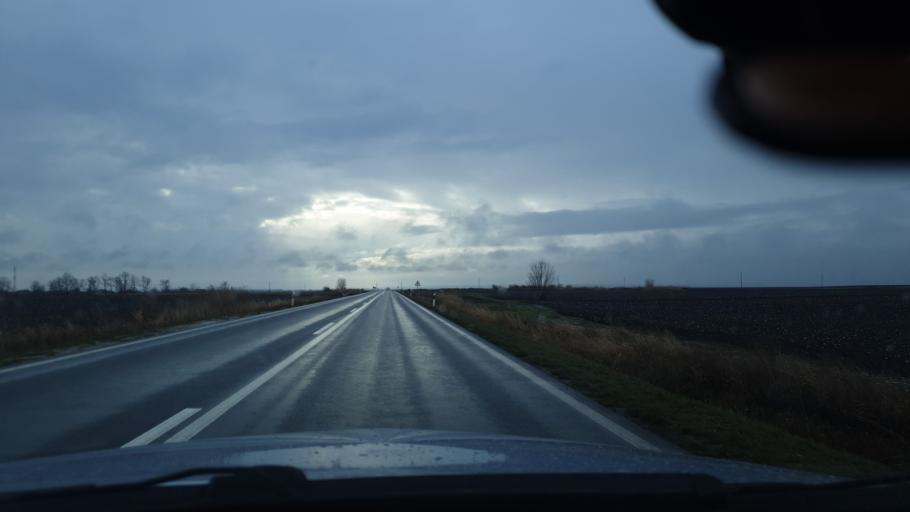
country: RS
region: Autonomna Pokrajina Vojvodina
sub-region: Juznobanatski Okrug
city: Kovin
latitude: 44.8182
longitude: 20.8540
